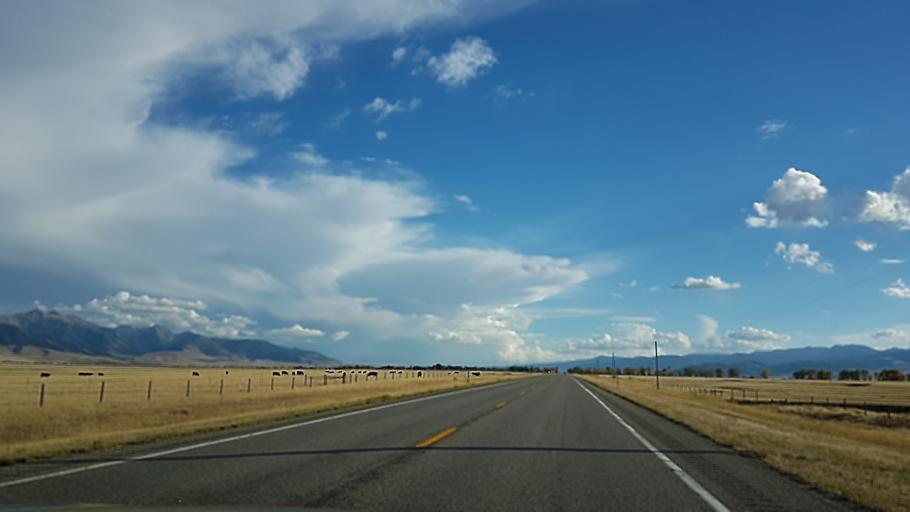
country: US
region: Montana
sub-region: Madison County
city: Virginia City
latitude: 45.2213
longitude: -111.6789
